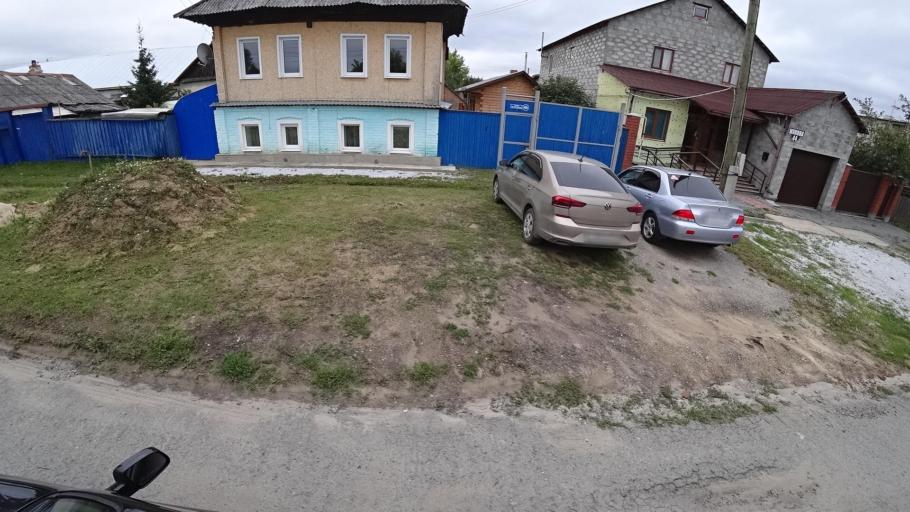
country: RU
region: Sverdlovsk
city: Kamyshlov
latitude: 56.8392
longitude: 62.7183
